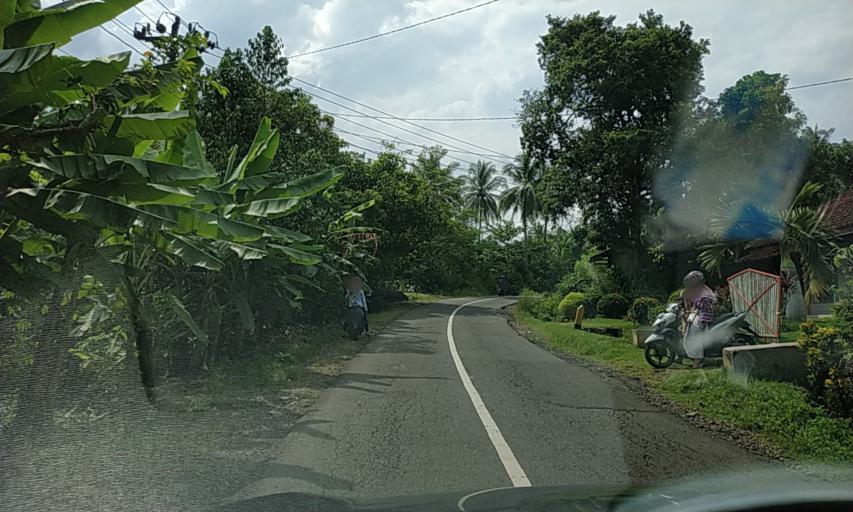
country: ID
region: Central Java
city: Winangun
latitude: -7.3702
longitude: 108.6992
